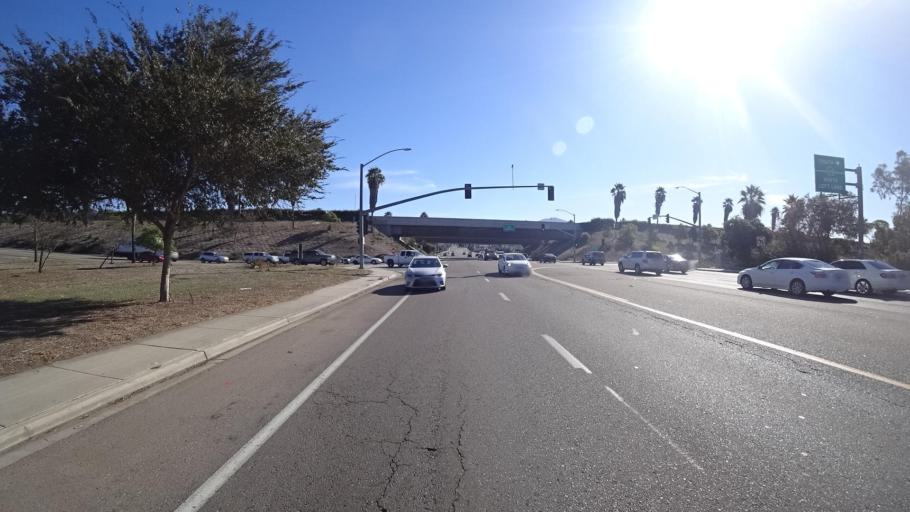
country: US
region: California
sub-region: San Diego County
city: La Presa
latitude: 32.7148
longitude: -117.0155
